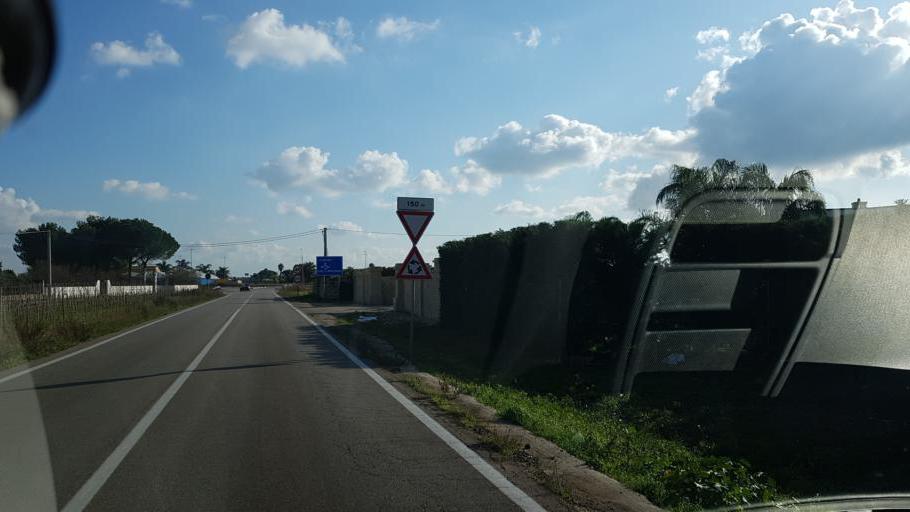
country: IT
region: Apulia
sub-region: Provincia di Lecce
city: Leverano
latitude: 40.3072
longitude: 17.9884
